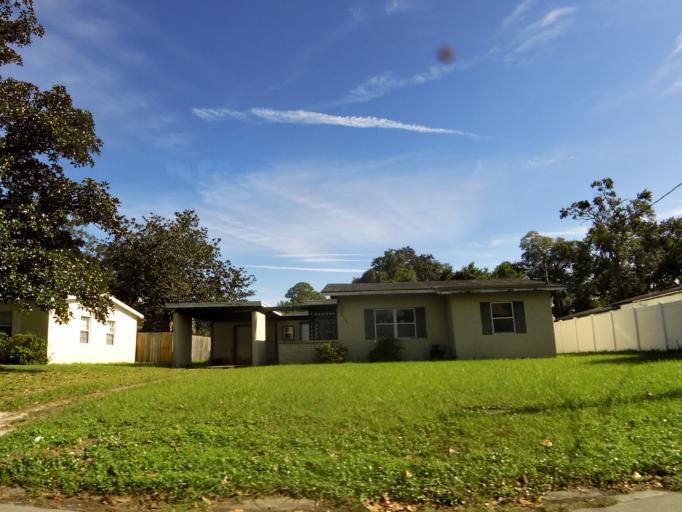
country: US
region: Florida
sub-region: Duval County
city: Jacksonville
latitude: 30.2588
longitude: -81.6368
